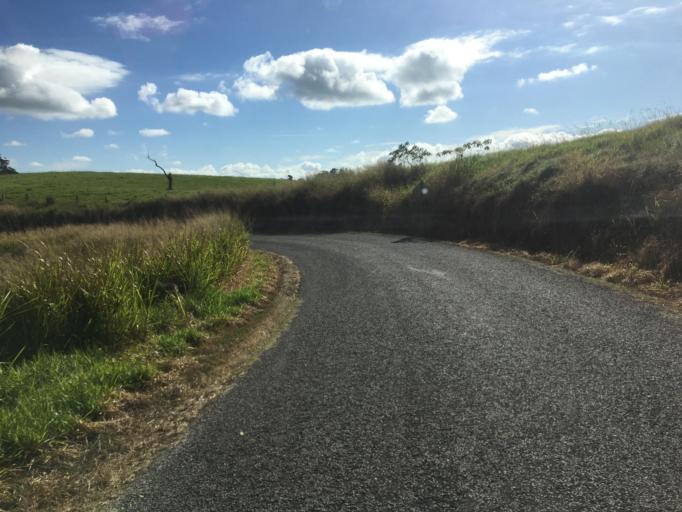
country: AU
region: Queensland
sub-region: Tablelands
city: Ravenshoe
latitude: -17.5371
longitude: 145.6103
